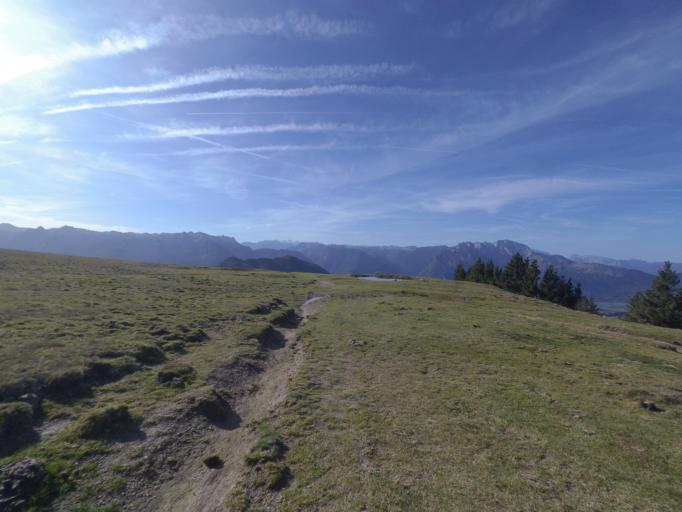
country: AT
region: Salzburg
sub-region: Politischer Bezirk Salzburg-Umgebung
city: Hintersee
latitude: 47.6385
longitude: 13.2682
